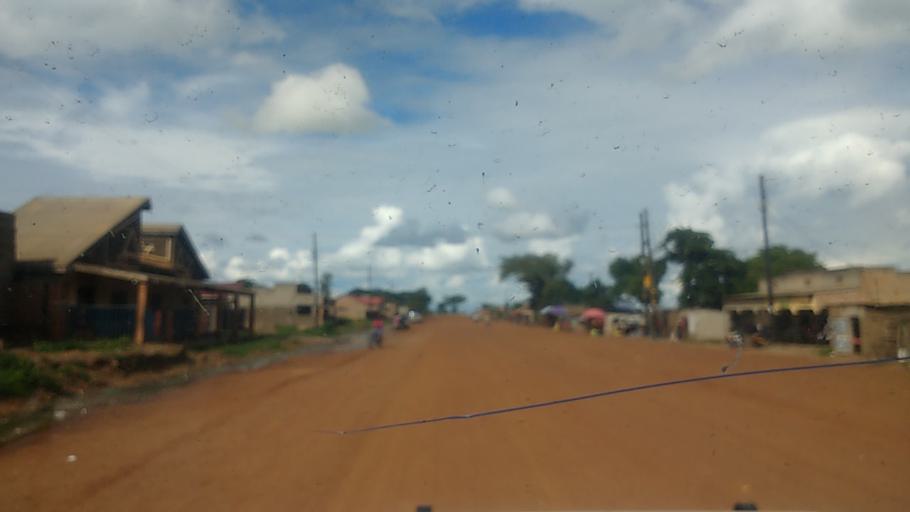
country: UG
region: Eastern Region
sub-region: Katakwi District
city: Katakwi
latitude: 1.9198
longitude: 33.9864
